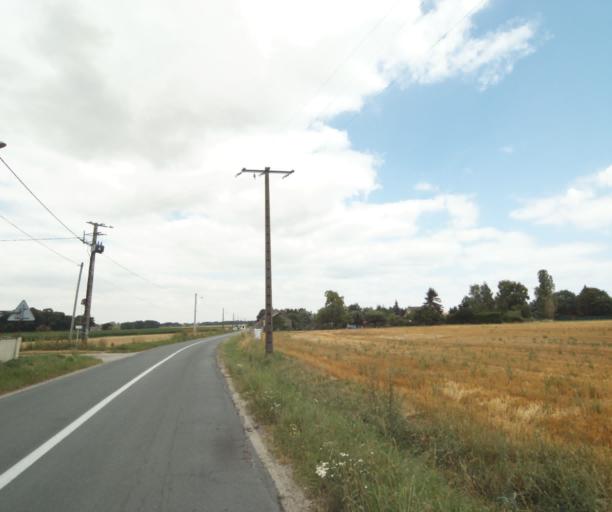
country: FR
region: Centre
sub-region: Departement du Loiret
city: Boigny-sur-Bionne
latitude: 47.9223
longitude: 2.0441
